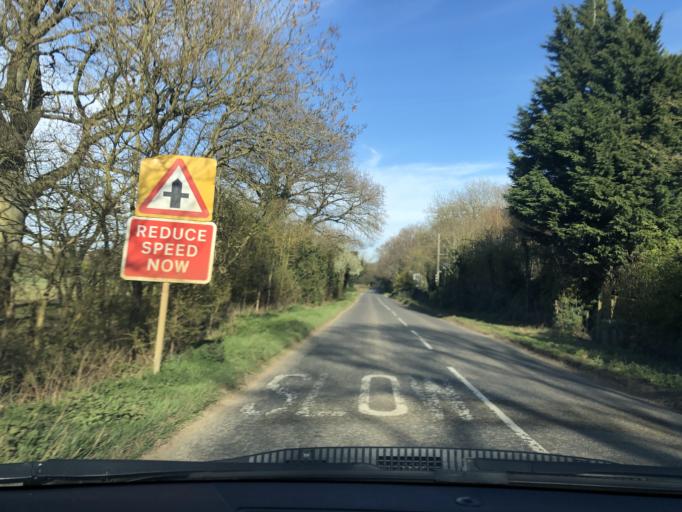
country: GB
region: England
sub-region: Oxfordshire
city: Hook Norton
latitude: 52.0136
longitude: -1.4427
